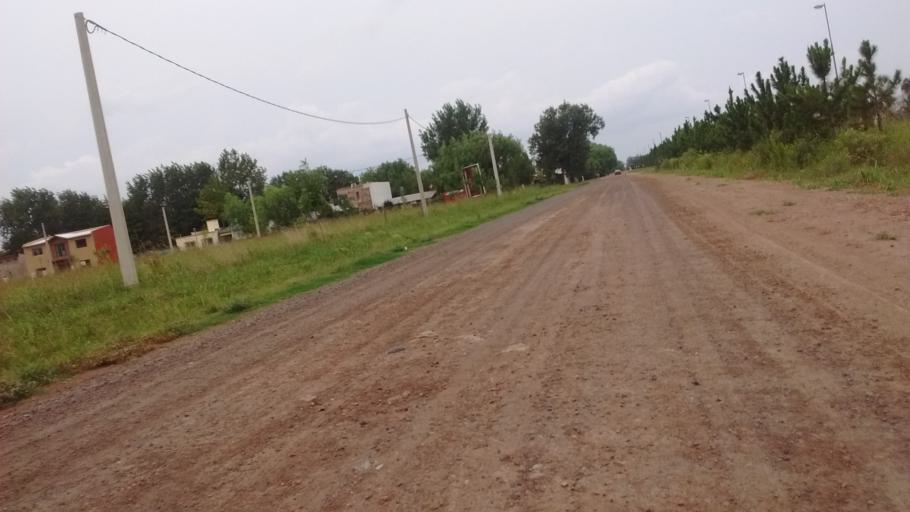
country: AR
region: Santa Fe
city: Funes
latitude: -32.9246
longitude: -60.8501
